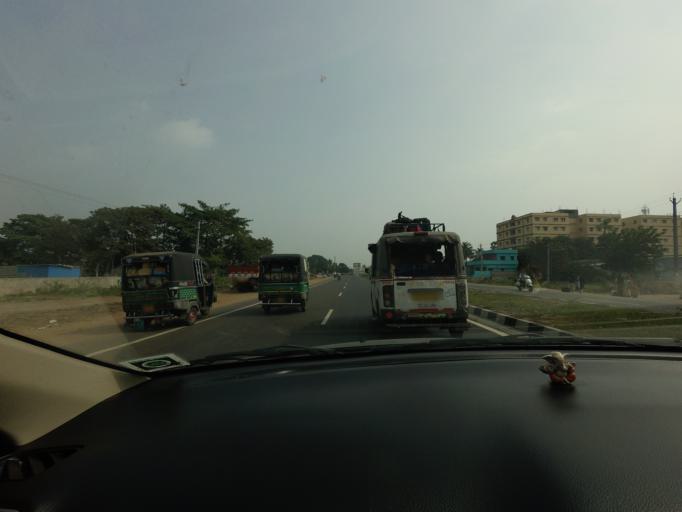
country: IN
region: Andhra Pradesh
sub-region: Krishna
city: Kankipadu
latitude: 16.4680
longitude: 80.7277
